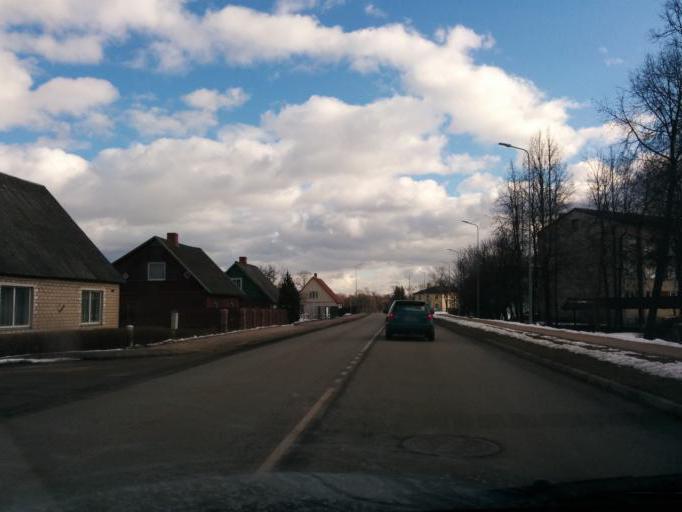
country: LV
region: Balvu Rajons
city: Balvi
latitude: 57.1399
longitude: 27.2497
